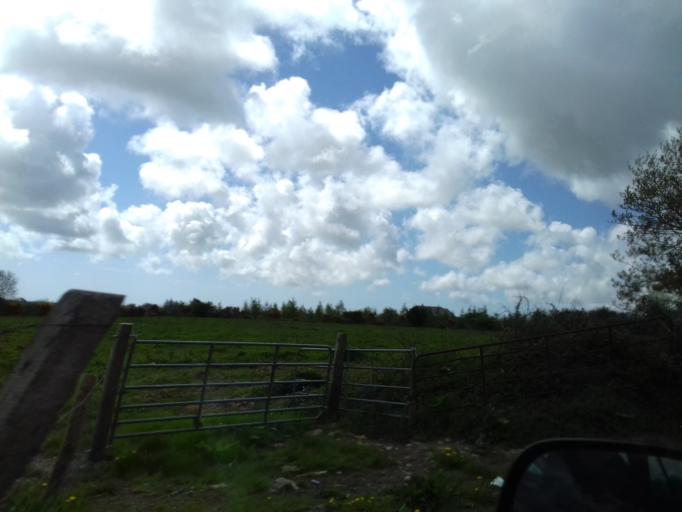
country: IE
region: Leinster
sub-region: Loch Garman
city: Loch Garman
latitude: 52.3131
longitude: -6.5291
